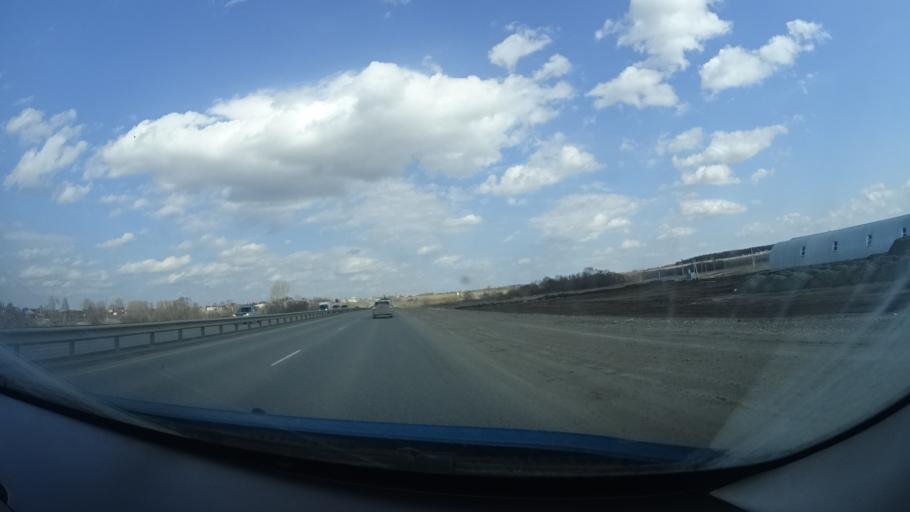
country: RU
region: Perm
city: Kultayevo
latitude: 57.9025
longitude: 55.9786
